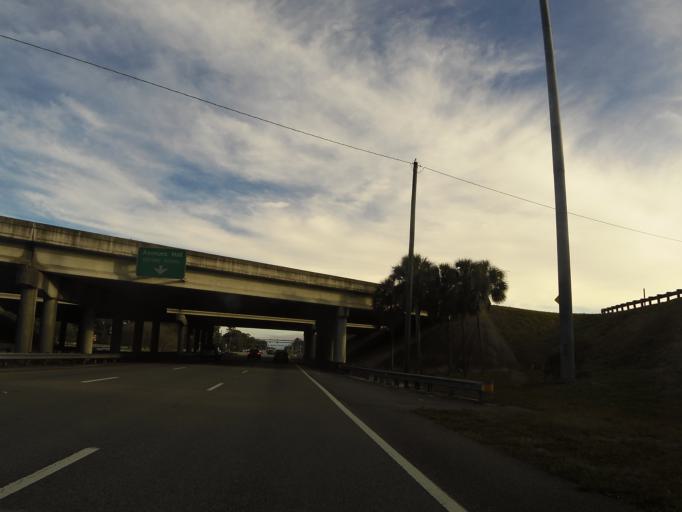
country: US
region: Florida
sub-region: Saint Johns County
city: Fruit Cove
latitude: 30.1851
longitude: -81.5589
